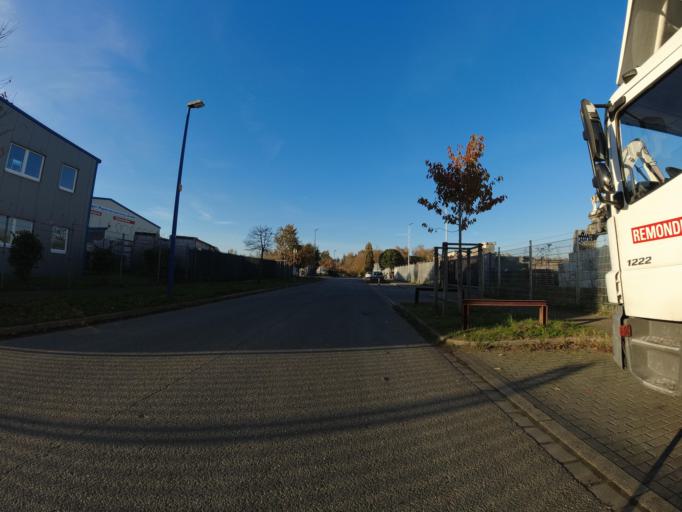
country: DE
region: North Rhine-Westphalia
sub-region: Regierungsbezirk Dusseldorf
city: Hochfeld
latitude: 51.3834
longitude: 6.6875
